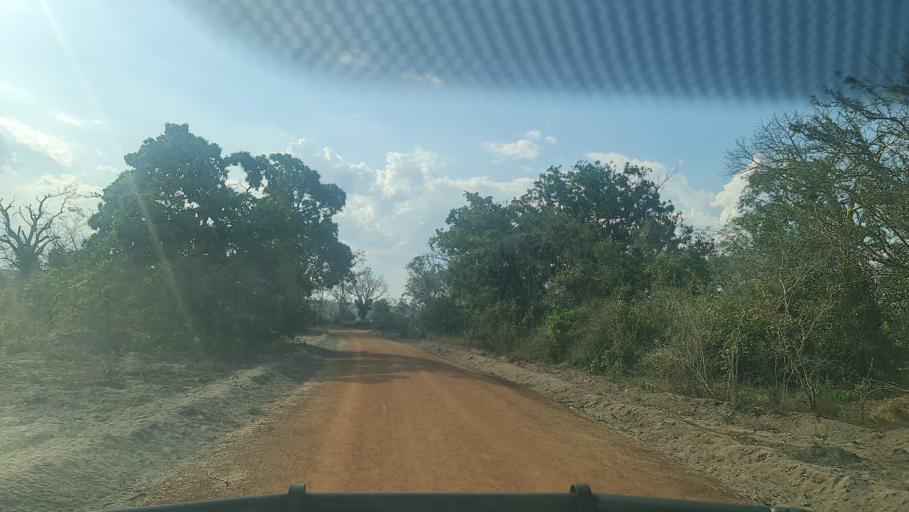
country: MZ
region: Nampula
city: Ilha de Mocambique
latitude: -15.5014
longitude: 40.1614
